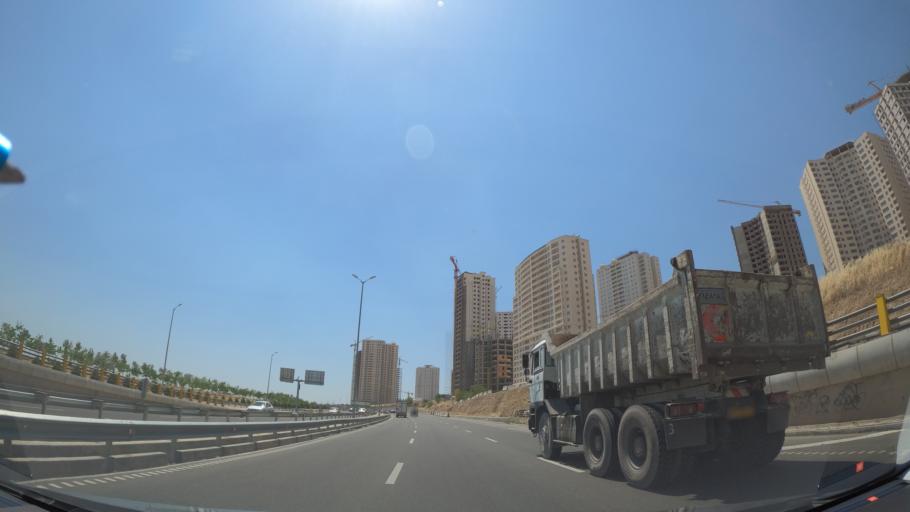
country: IR
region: Tehran
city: Shahr-e Qods
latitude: 35.7522
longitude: 51.1415
